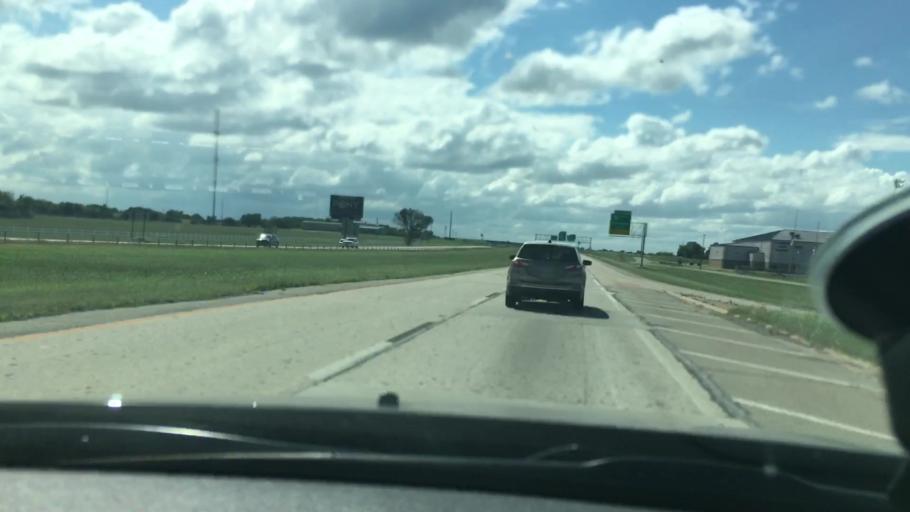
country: US
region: Oklahoma
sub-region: McIntosh County
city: Checotah
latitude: 35.4582
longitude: -95.5320
